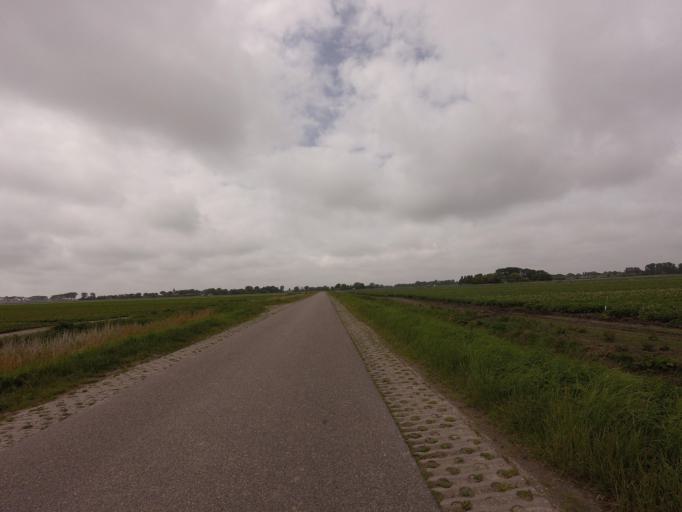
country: NL
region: North Holland
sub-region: Gemeente Schagen
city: Schagen
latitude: 52.7715
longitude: 4.7830
